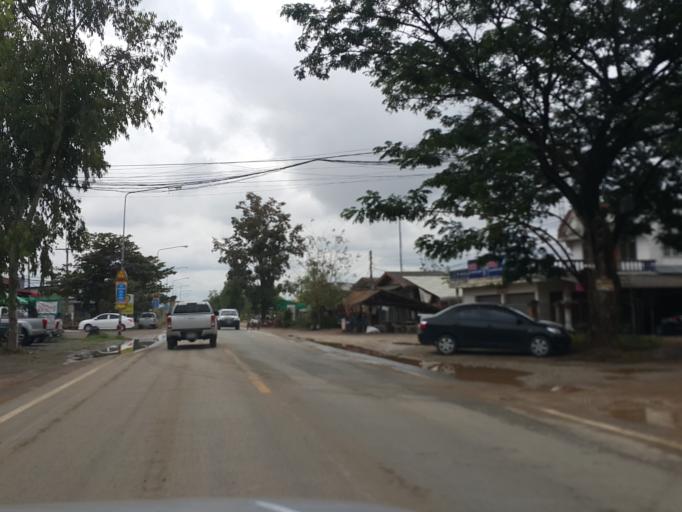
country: TH
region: Lamphun
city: Ban Thi
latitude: 18.5903
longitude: 99.0810
